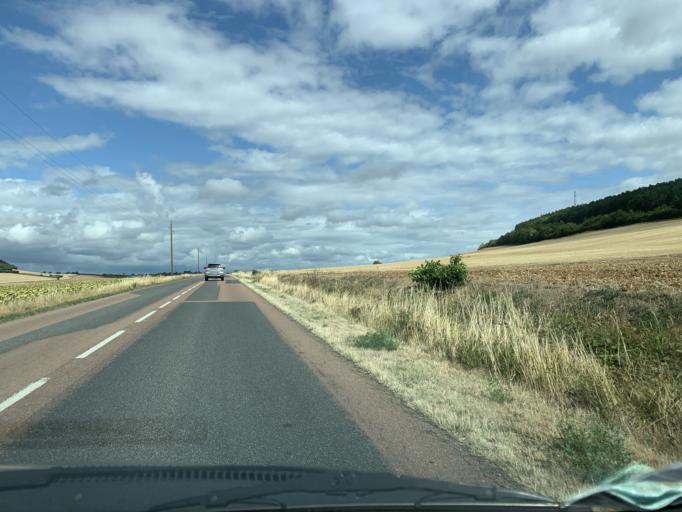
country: FR
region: Bourgogne
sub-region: Departement de la Nievre
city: Varzy
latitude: 47.3664
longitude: 3.4127
